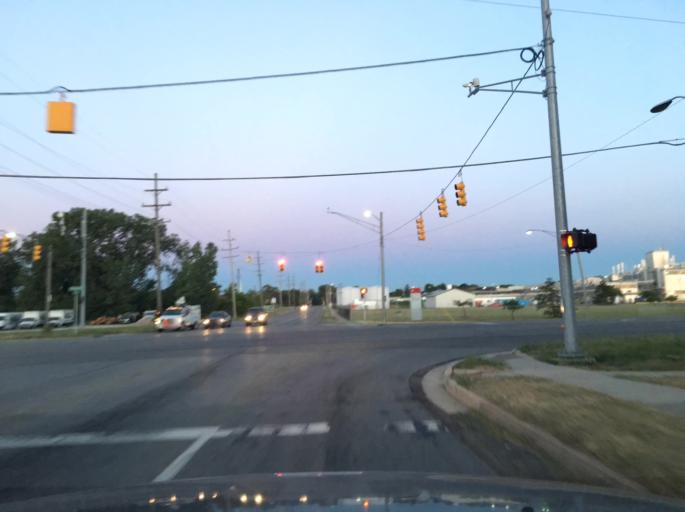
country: US
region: Michigan
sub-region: Macomb County
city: Mount Clemens
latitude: 42.6160
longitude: -82.8870
